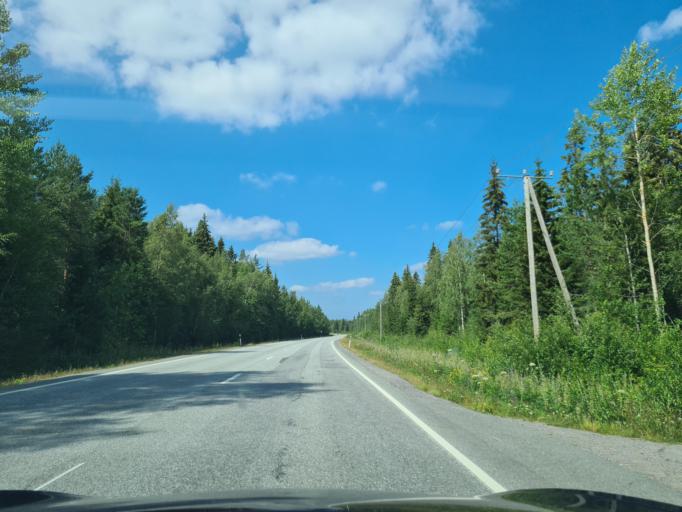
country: FI
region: Ostrobothnia
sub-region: Vaasa
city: Vaasa
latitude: 63.1741
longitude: 21.5789
